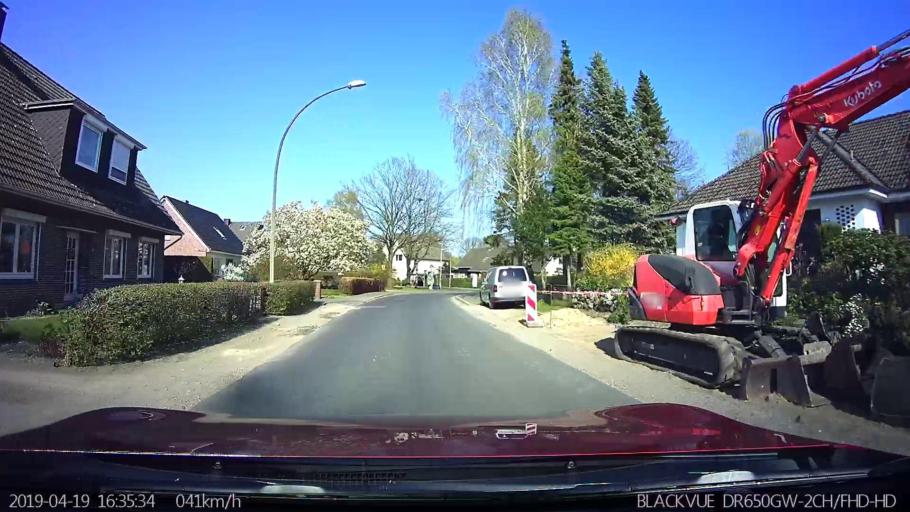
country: DE
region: Schleswig-Holstein
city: Tangstedt
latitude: 53.6690
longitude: 9.8399
